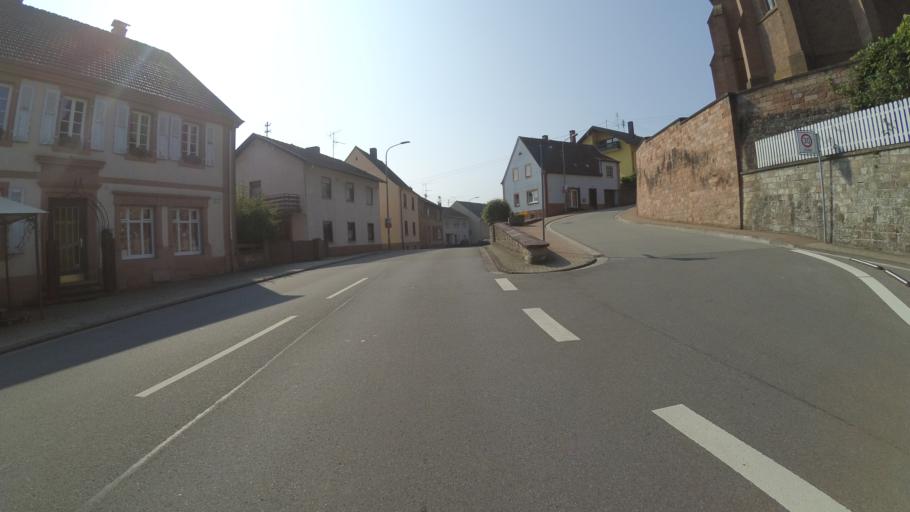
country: DE
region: Rheinland-Pfalz
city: Rieschweiler-Muhlbach
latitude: 49.2466
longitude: 7.5041
